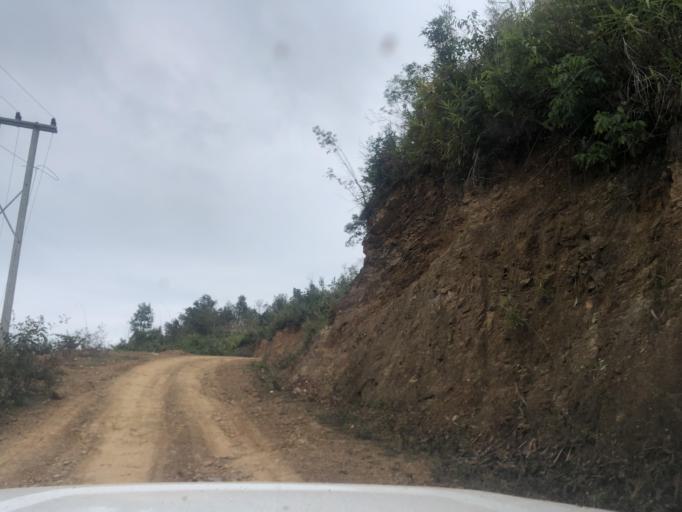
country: LA
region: Phongsali
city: Khoa
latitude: 21.2551
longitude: 102.5899
